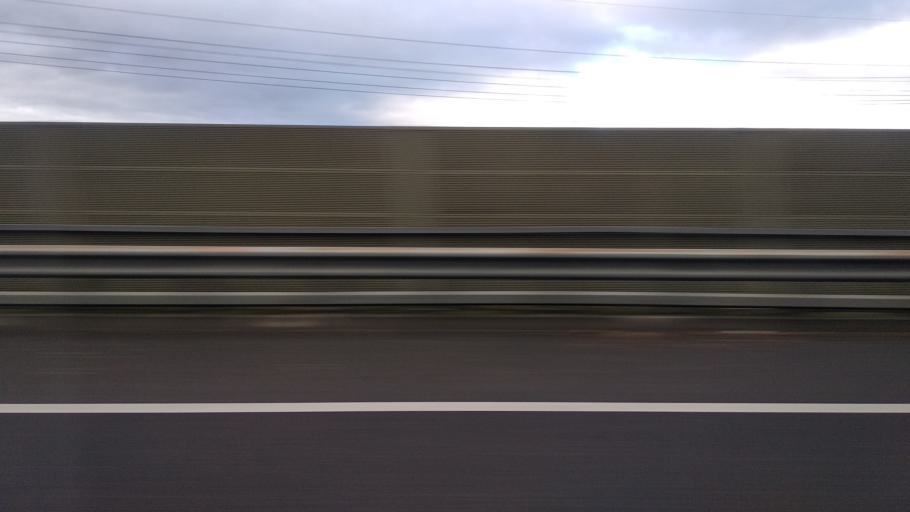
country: AT
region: Vorarlberg
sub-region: Politischer Bezirk Bregenz
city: Lauterach
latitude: 47.4830
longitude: 9.7415
